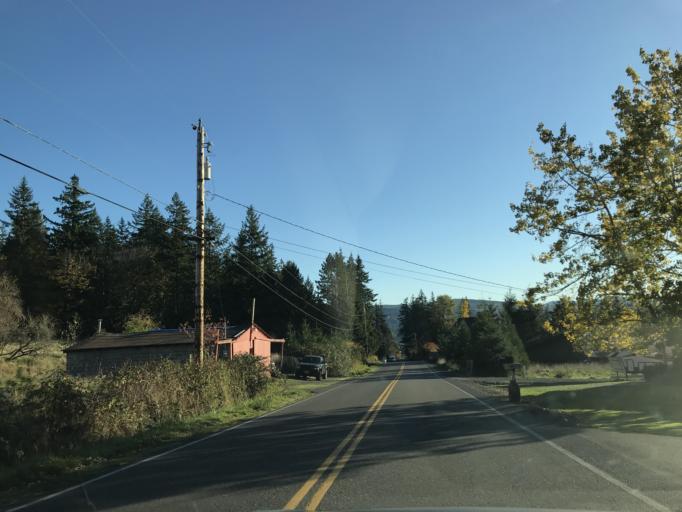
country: US
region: Washington
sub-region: Whatcom County
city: Geneva
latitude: 48.7761
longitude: -122.4032
